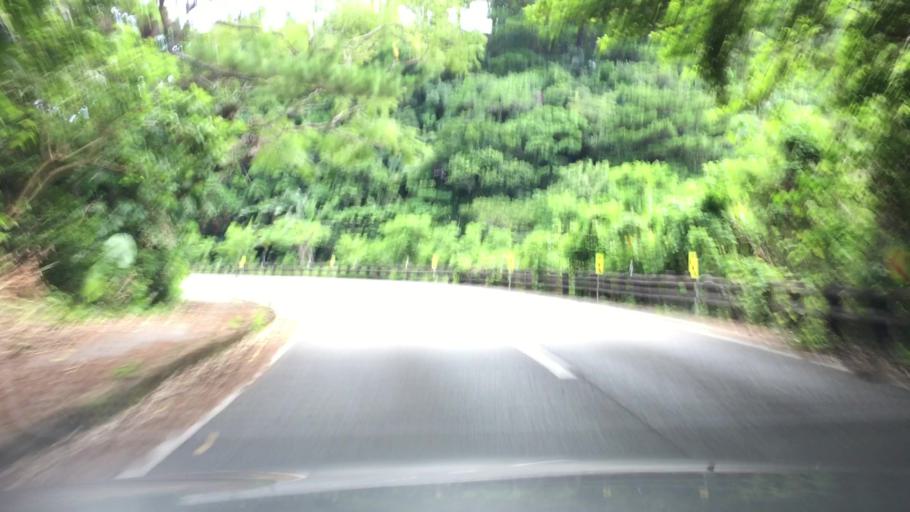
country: JP
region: Okinawa
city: Ishigaki
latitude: 24.4564
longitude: 124.1381
